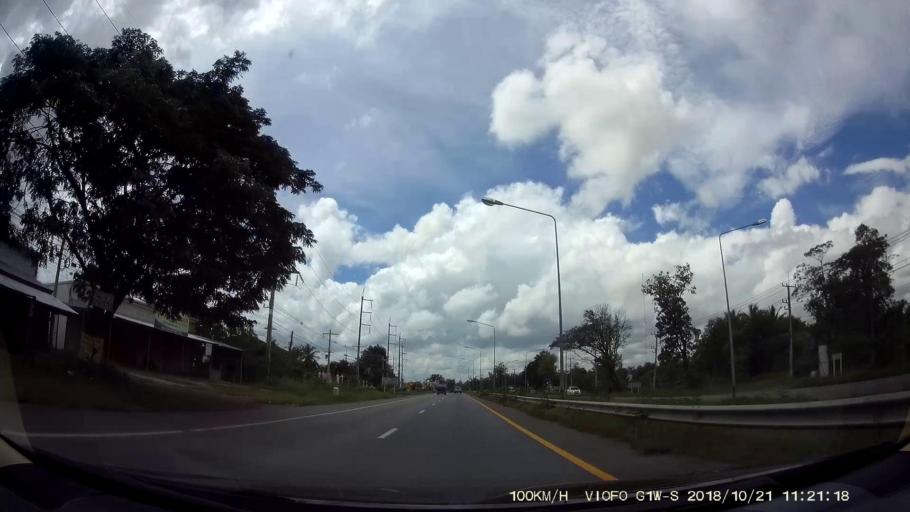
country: TH
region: Chaiyaphum
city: Chaiyaphum
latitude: 15.8480
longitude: 102.0664
